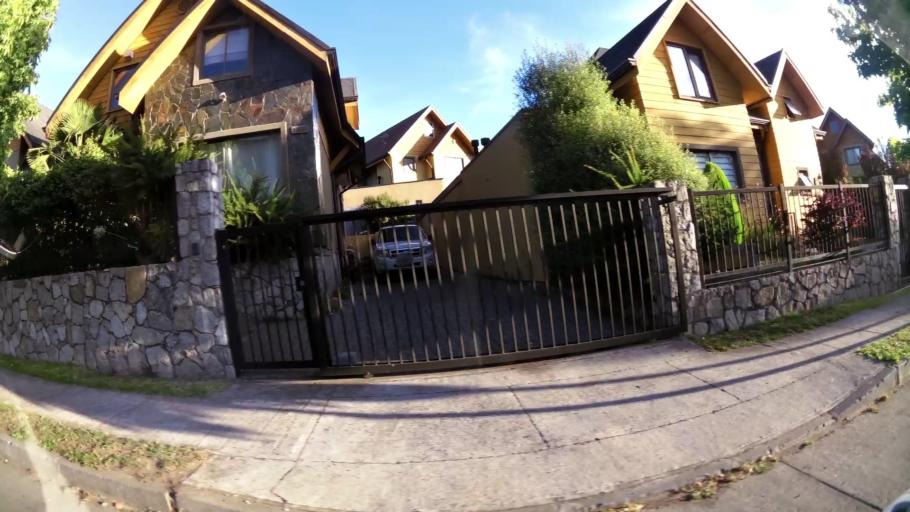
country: CL
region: Biobio
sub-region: Provincia de Concepcion
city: Concepcion
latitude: -36.8579
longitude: -73.1007
